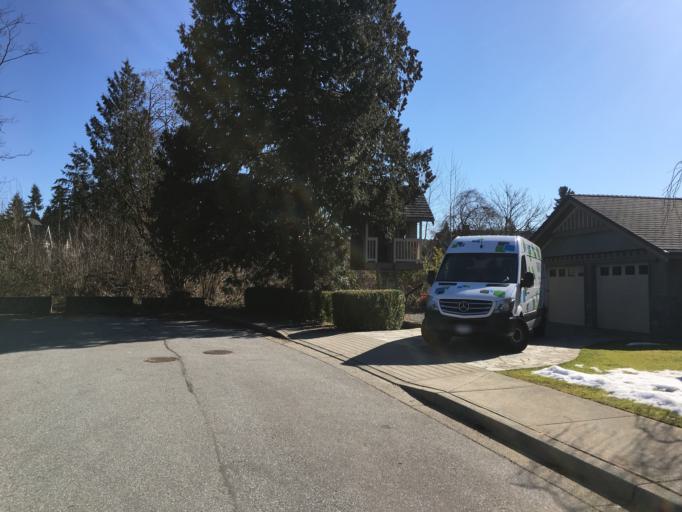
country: CA
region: British Columbia
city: Port Moody
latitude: 49.2689
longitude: -122.8890
